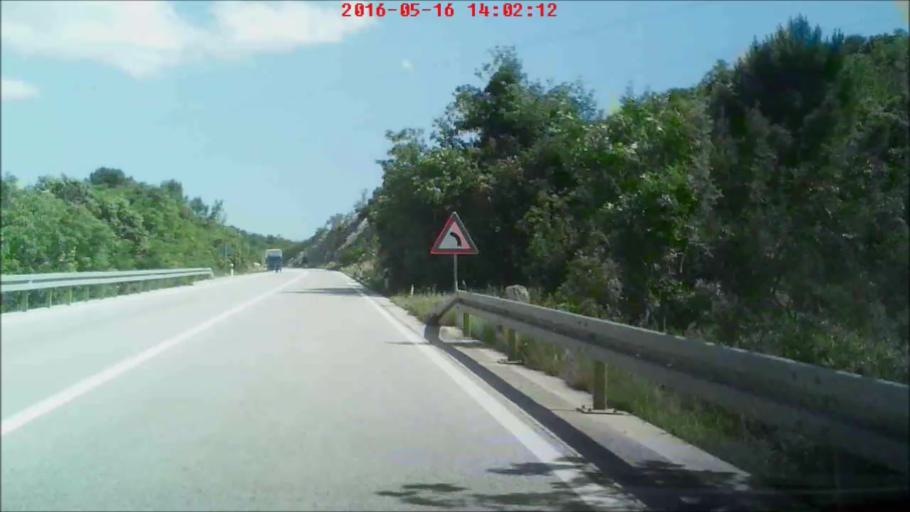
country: HR
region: Dubrovacko-Neretvanska
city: Ston
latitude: 42.8267
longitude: 17.7558
